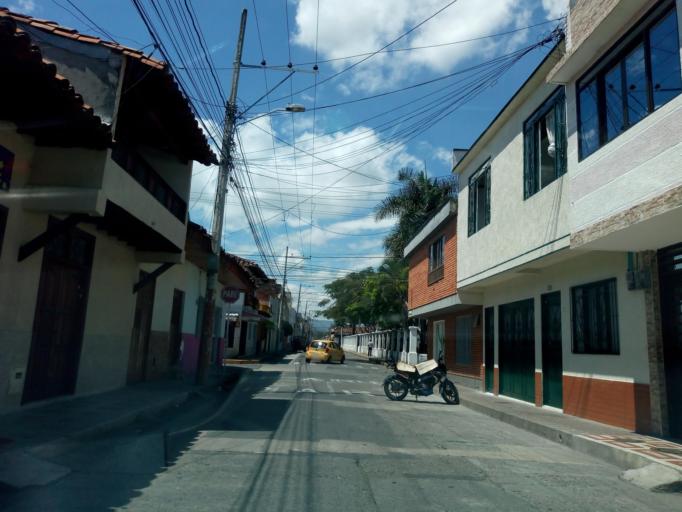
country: CO
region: Valle del Cauca
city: Cartago
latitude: 4.7487
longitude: -75.9092
